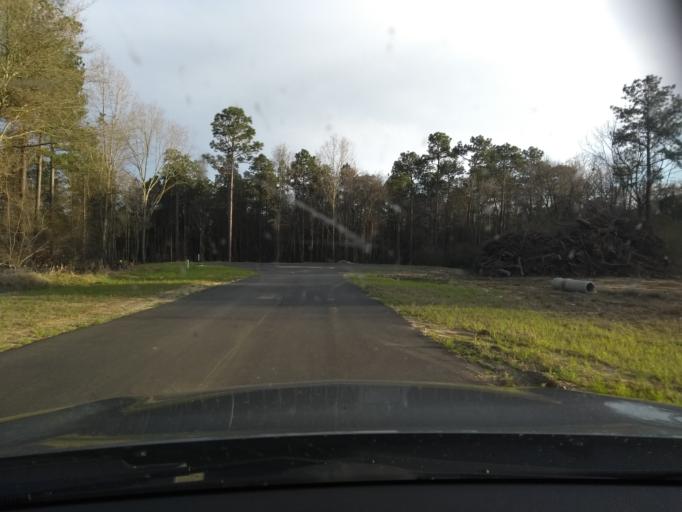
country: US
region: Georgia
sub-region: Bulloch County
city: Statesboro
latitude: 32.3553
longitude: -81.7672
